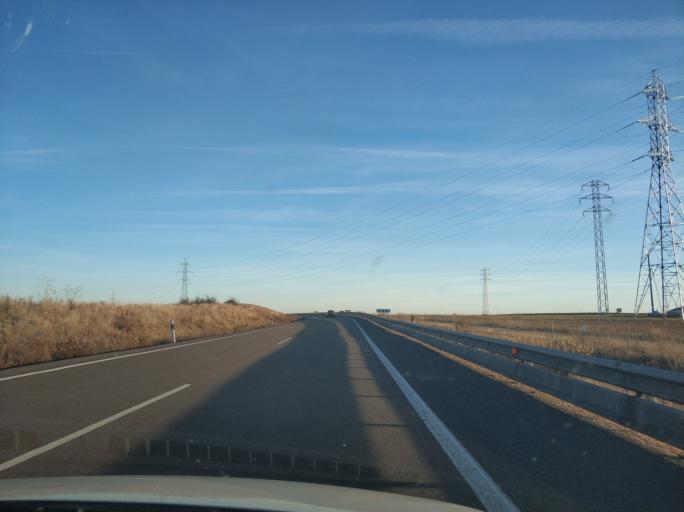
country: ES
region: Castille and Leon
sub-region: Provincia de Valladolid
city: Tordesillas
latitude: 41.5089
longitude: -4.9896
